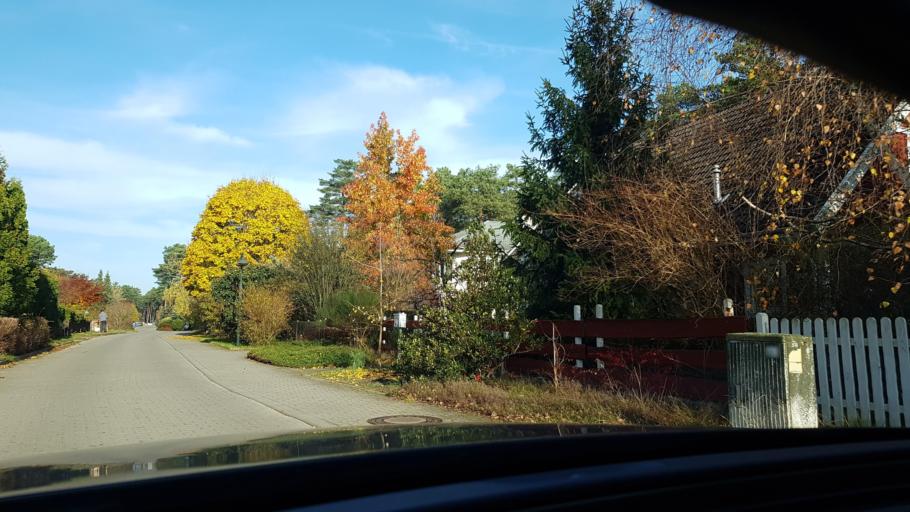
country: DE
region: Brandenburg
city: Borkwalde
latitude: 52.2557
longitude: 12.8424
